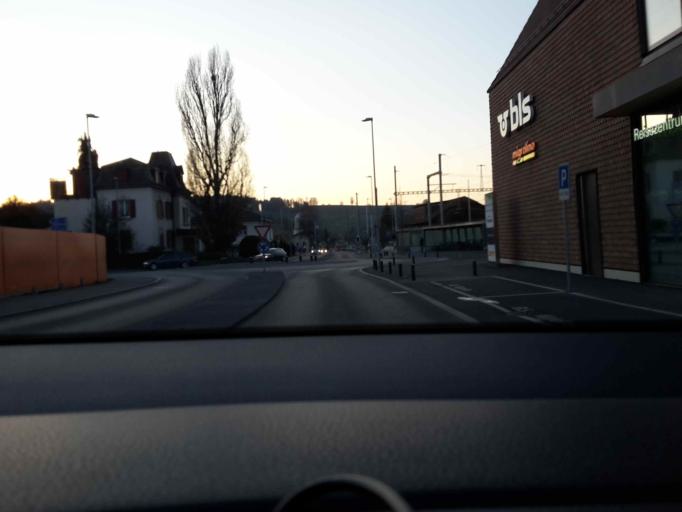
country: CH
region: Bern
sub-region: Oberaargau
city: Huttwil
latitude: 47.1142
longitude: 7.8425
